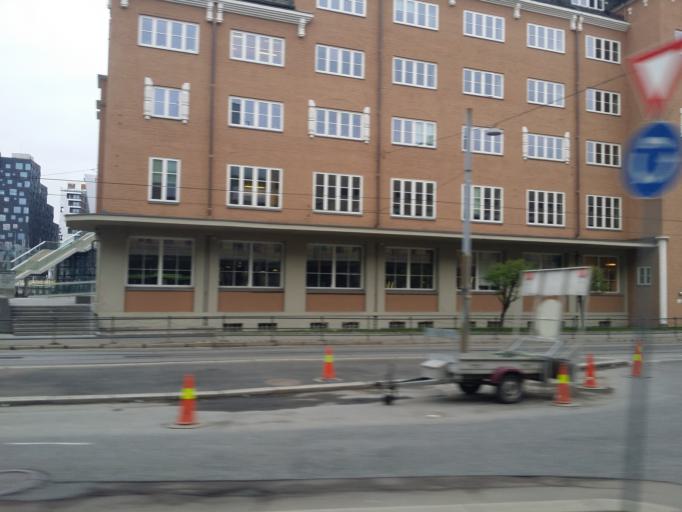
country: NO
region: Oslo
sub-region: Oslo
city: Oslo
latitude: 59.9110
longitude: 10.7604
